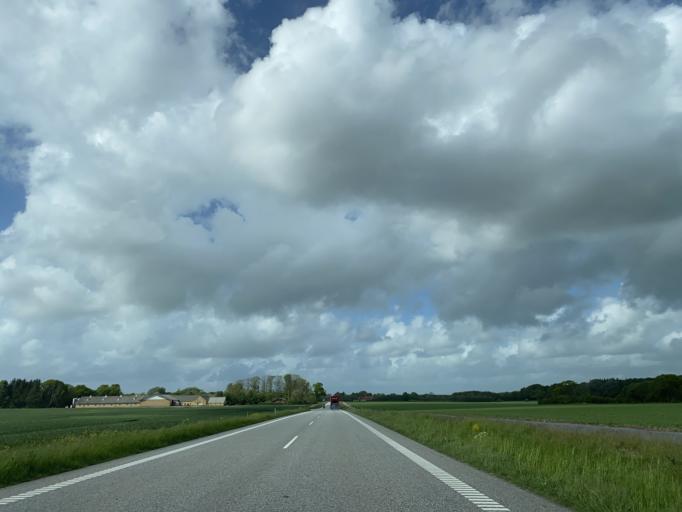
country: DK
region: South Denmark
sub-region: Kolding Kommune
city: Christiansfeld
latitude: 55.4076
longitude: 9.4780
